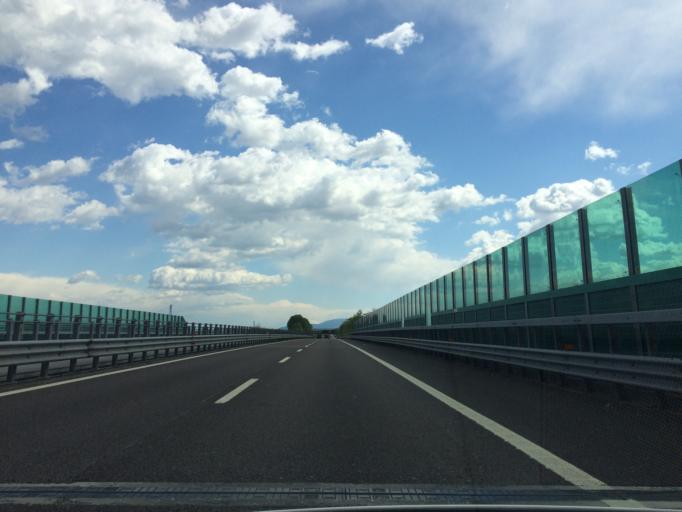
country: IT
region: Veneto
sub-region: Provincia di Vicenza
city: Marola
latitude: 45.5399
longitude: 11.6246
